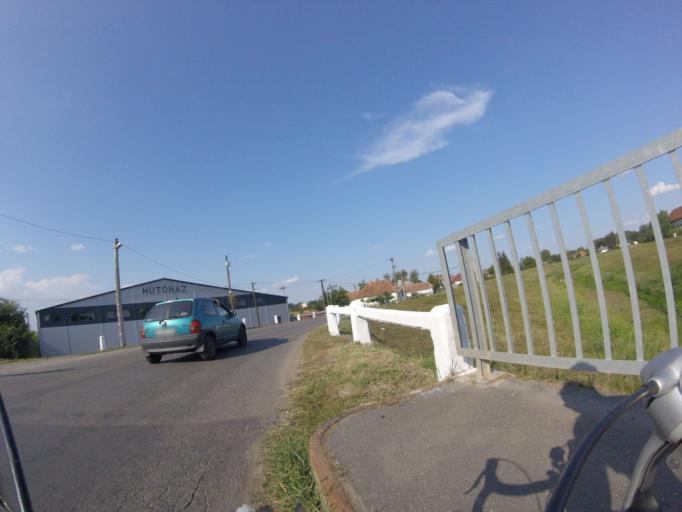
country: HU
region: Szabolcs-Szatmar-Bereg
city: Demecser
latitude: 48.1077
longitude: 21.9123
